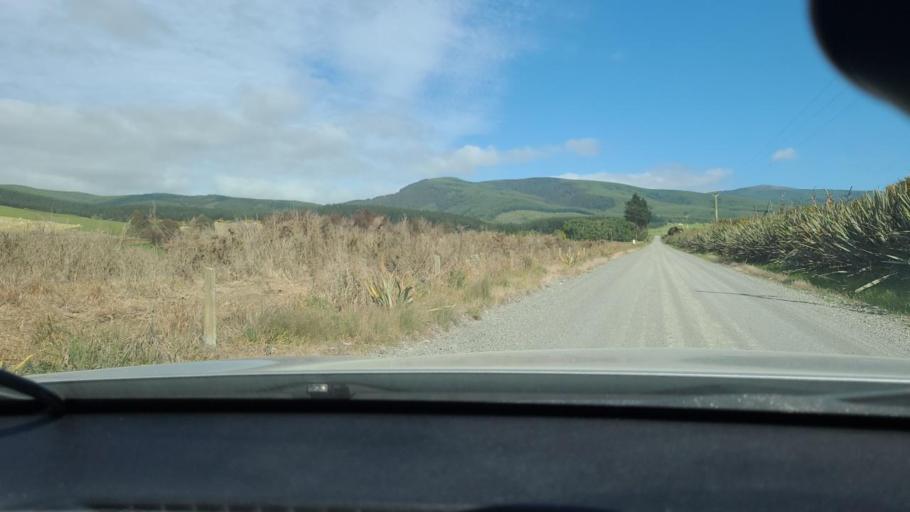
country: NZ
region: Southland
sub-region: Southland District
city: Winton
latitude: -45.8953
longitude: 168.0990
